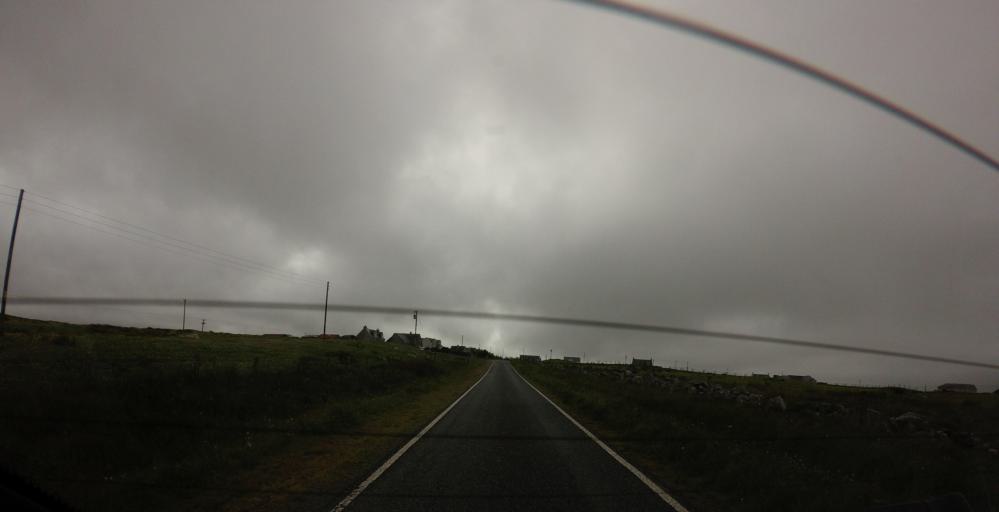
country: GB
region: Scotland
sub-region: Eilean Siar
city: Isle of North Uist
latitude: 57.6484
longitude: -7.3490
